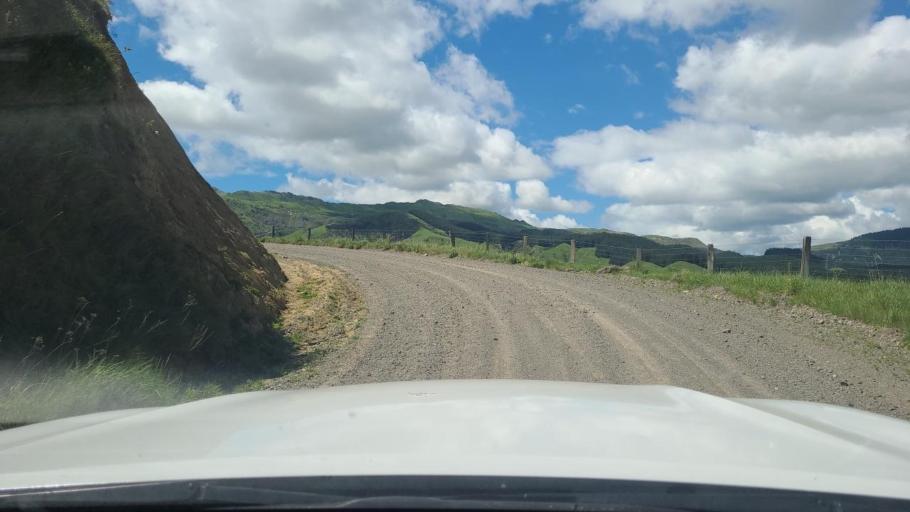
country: NZ
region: Hawke's Bay
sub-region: Napier City
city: Napier
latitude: -39.1630
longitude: 176.6656
